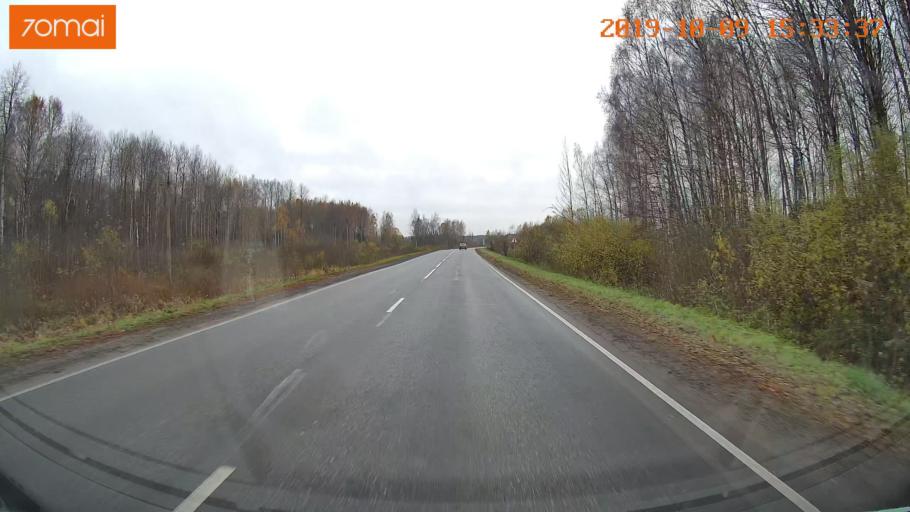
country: RU
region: Kostroma
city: Oktyabr'skiy
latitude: 57.9493
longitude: 41.2599
